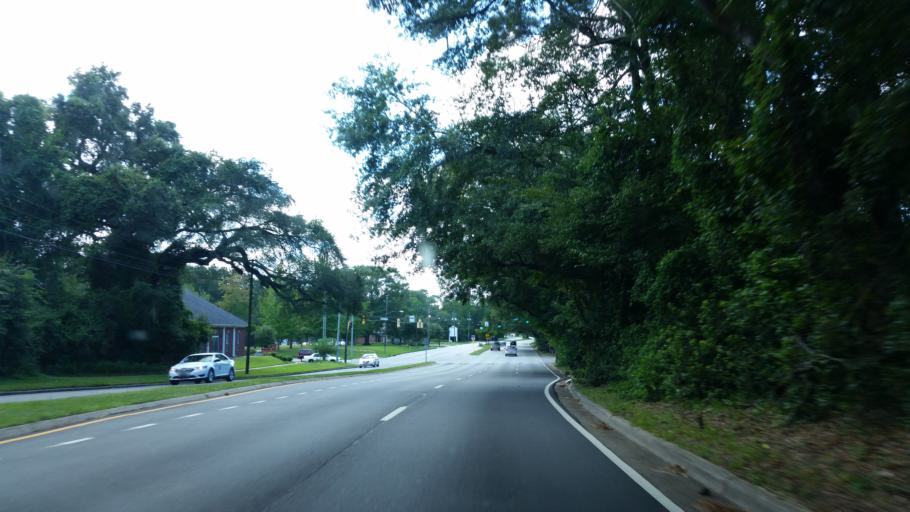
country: US
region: Alabama
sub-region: Mobile County
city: Mobile
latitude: 30.6764
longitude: -88.1041
